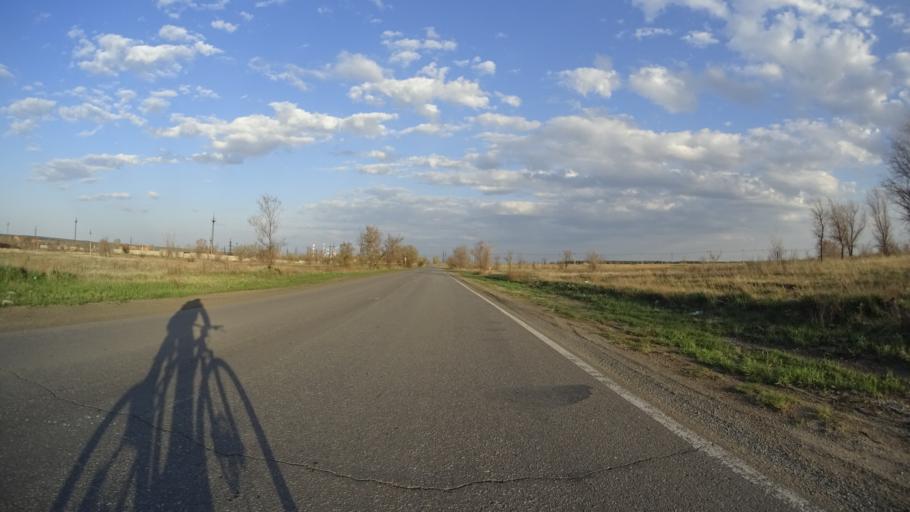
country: RU
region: Chelyabinsk
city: Troitsk
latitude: 54.0612
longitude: 61.5769
